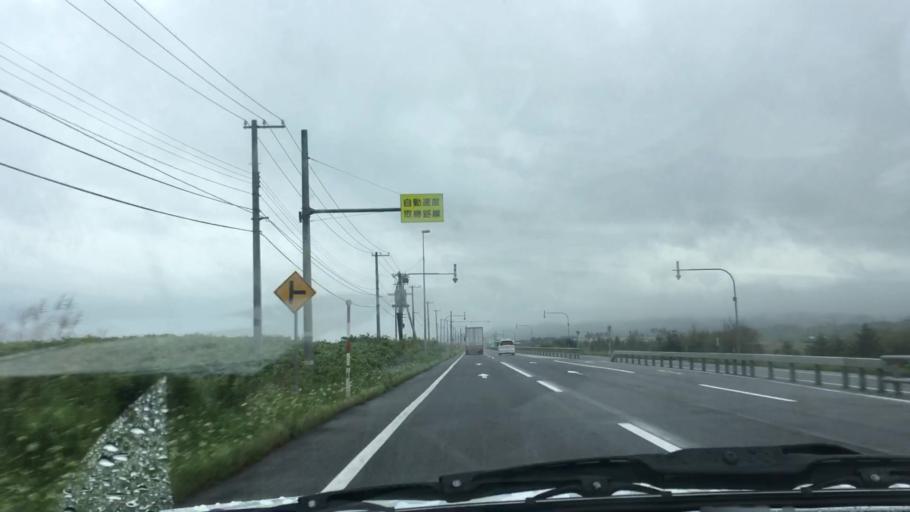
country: JP
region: Hokkaido
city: Niseko Town
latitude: 42.4007
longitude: 140.3032
